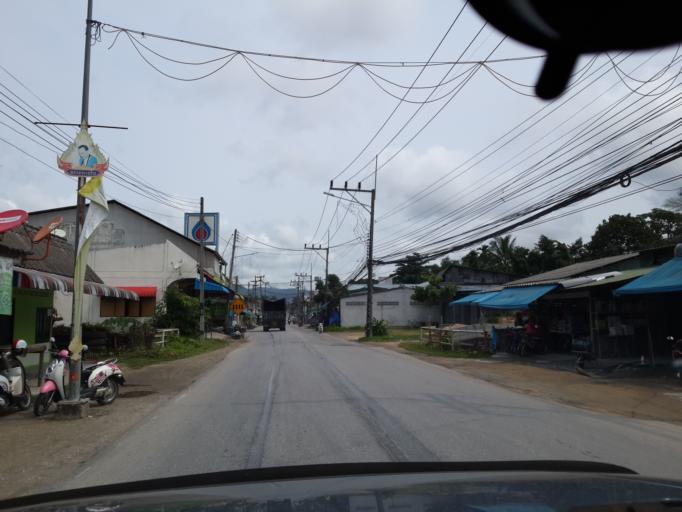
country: TH
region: Narathiwat
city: Rueso
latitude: 6.3905
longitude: 101.5157
